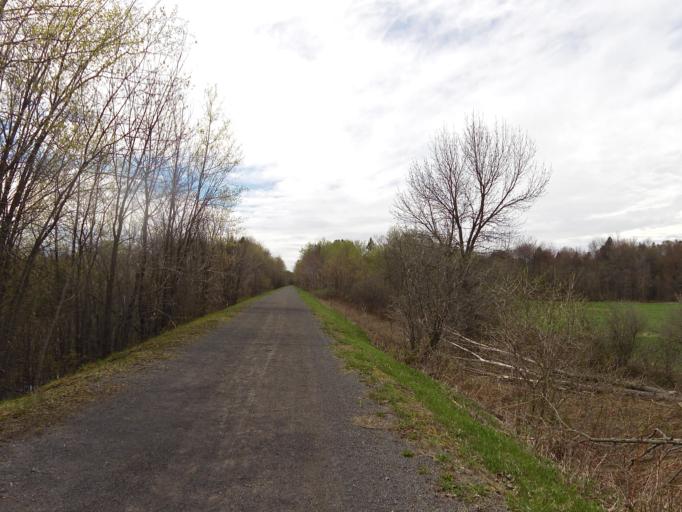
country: CA
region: Ontario
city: Hawkesbury
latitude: 45.5324
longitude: -74.6694
